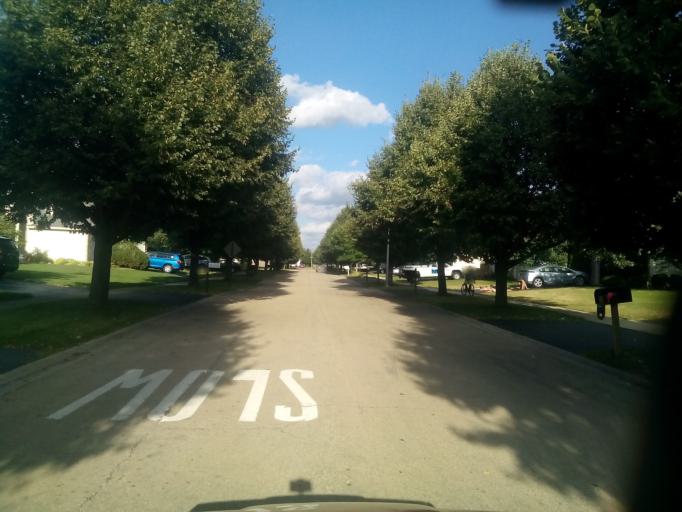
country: US
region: Illinois
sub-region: Will County
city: Plainfield
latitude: 41.6893
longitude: -88.1569
